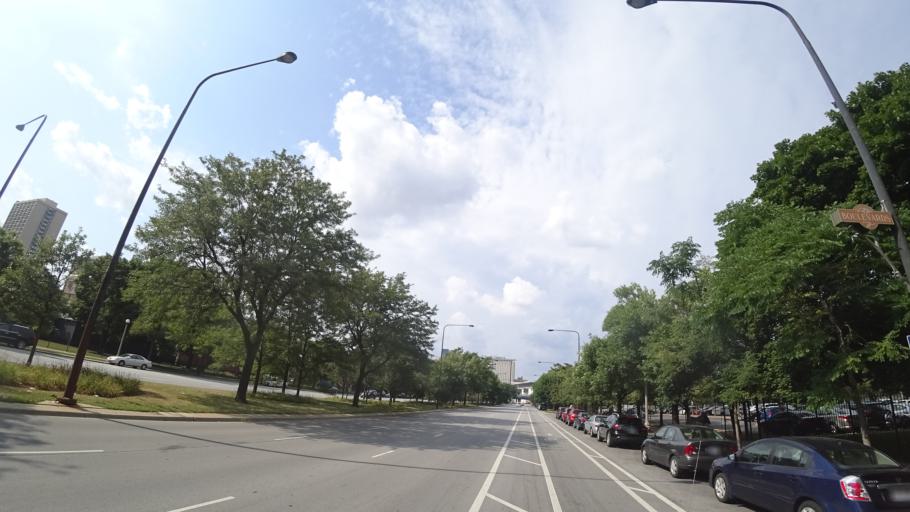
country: US
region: Illinois
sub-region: Cook County
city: Chicago
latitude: 41.8438
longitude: -87.6172
